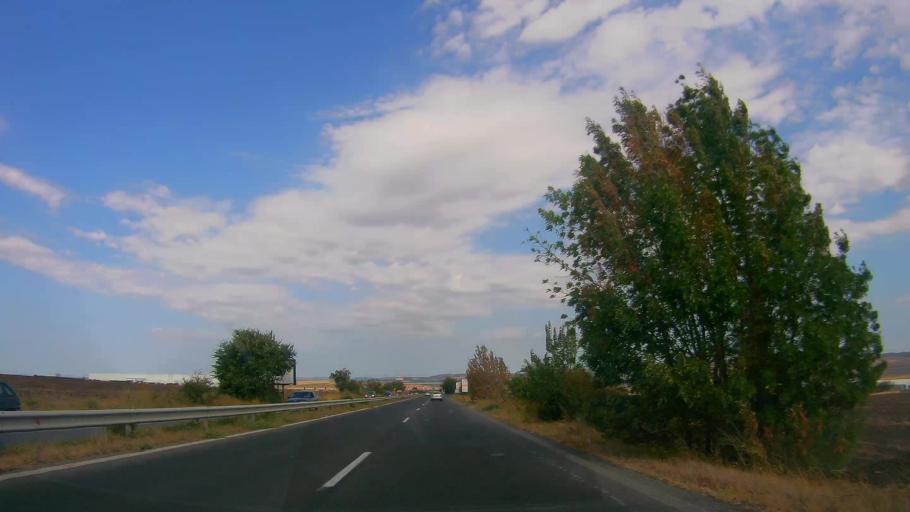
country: BG
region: Burgas
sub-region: Obshtina Burgas
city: Burgas
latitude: 42.5701
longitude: 27.4151
